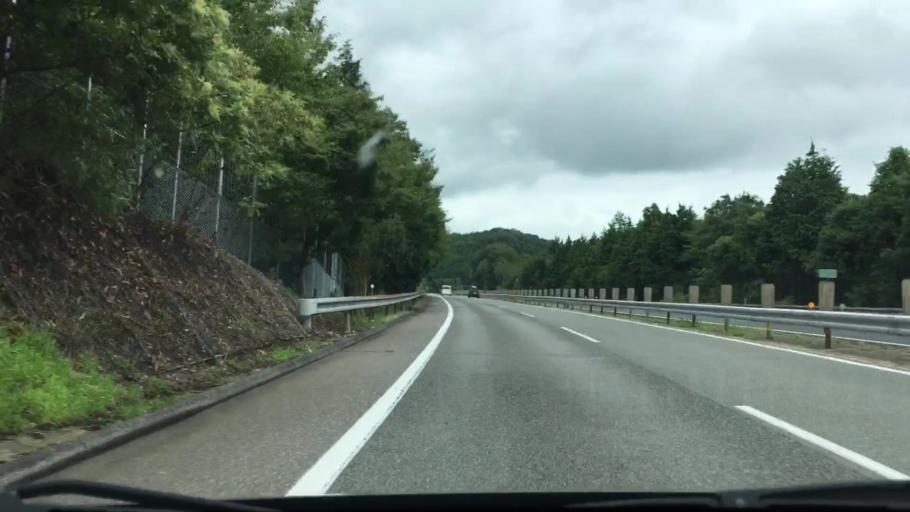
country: JP
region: Hiroshima
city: Miyoshi
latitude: 34.7585
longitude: 132.7771
